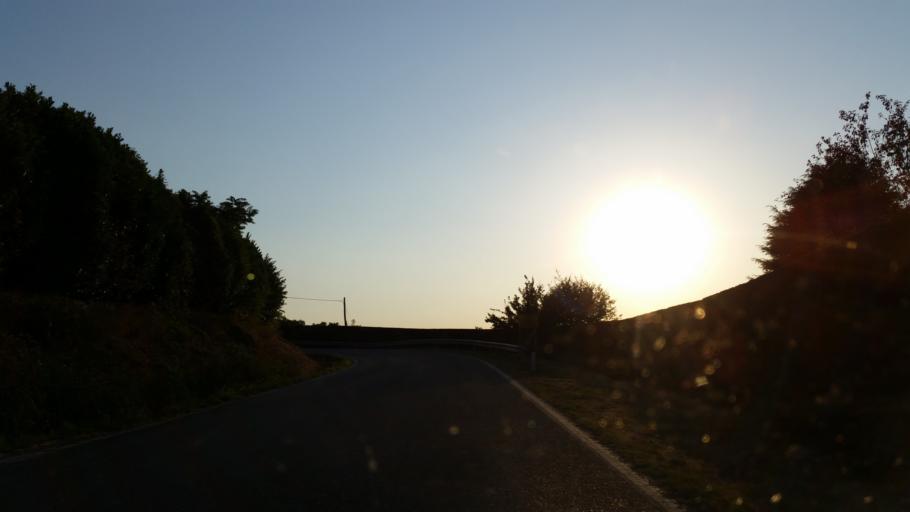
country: IT
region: Piedmont
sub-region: Provincia di Cuneo
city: Alba
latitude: 44.6892
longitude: 8.0445
